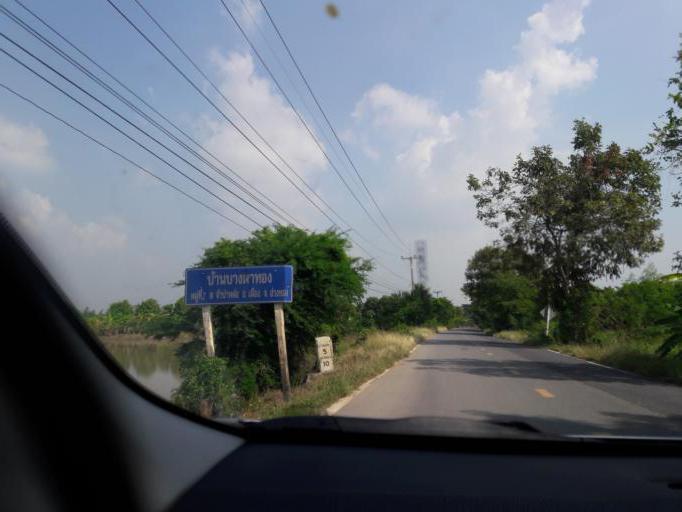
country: TH
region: Ang Thong
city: Ang Thong
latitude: 14.5442
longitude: 100.4130
